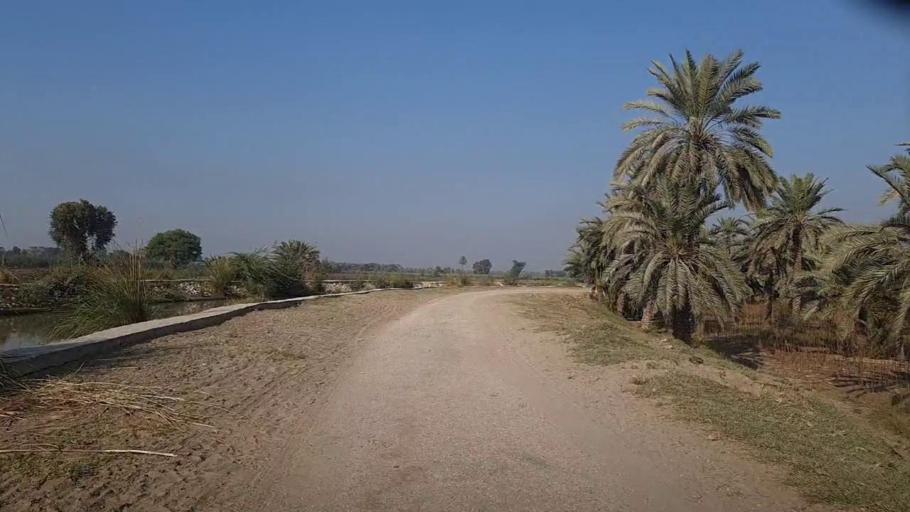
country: PK
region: Sindh
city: Ranipur
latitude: 27.2449
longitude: 68.5531
